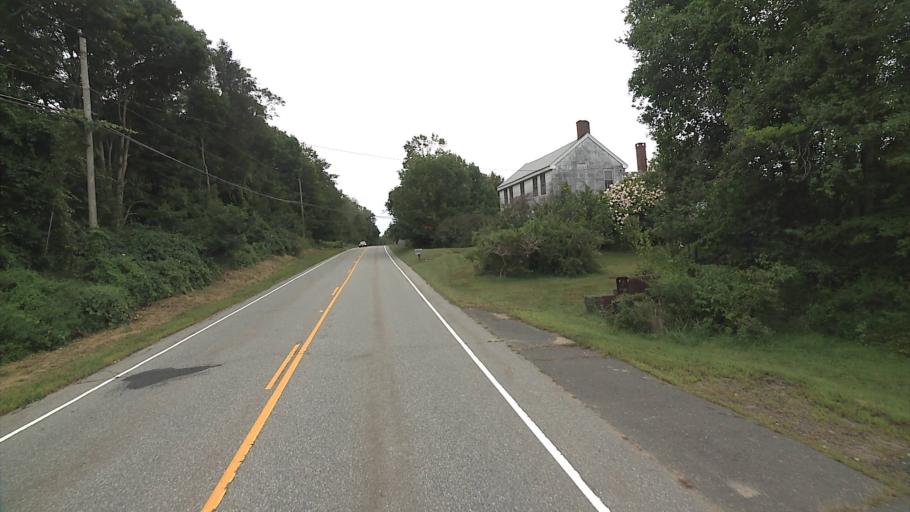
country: US
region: Connecticut
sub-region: Hartford County
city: Terramuggus
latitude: 41.7083
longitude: -72.4331
